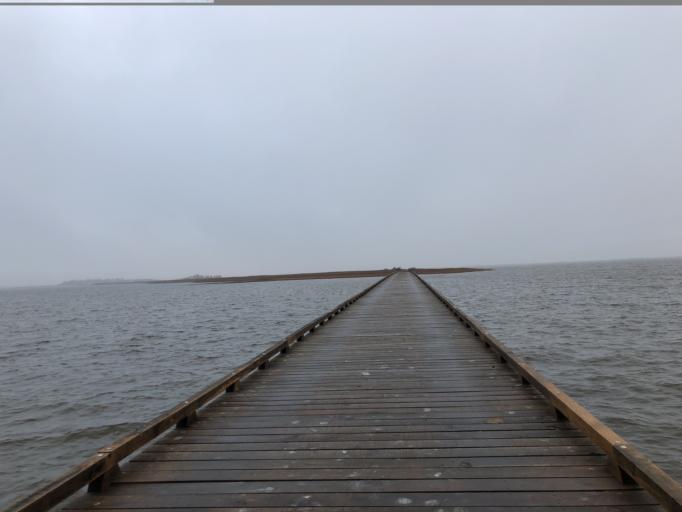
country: DK
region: Central Jutland
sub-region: Ringkobing-Skjern Kommune
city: Ringkobing
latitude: 56.1512
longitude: 8.2387
